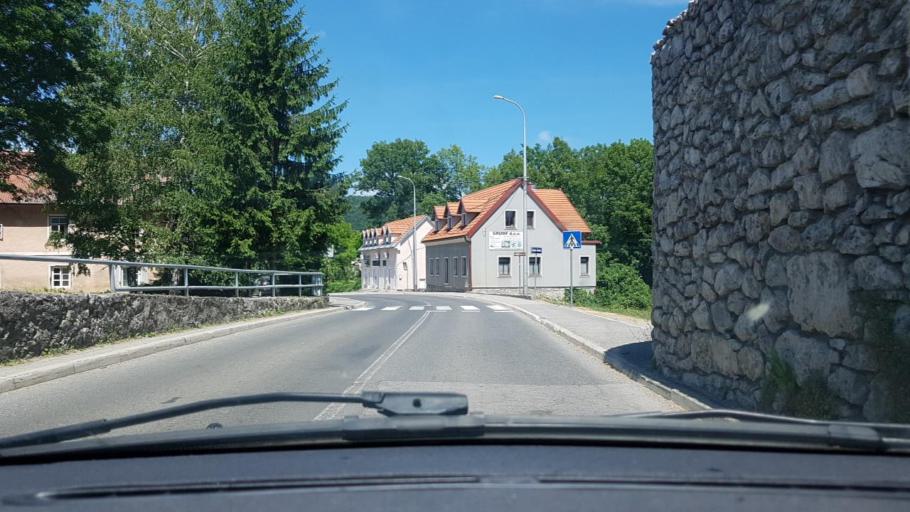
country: HR
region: Karlovacka
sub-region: Grad Ogulin
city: Ogulin
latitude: 45.2675
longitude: 15.2241
